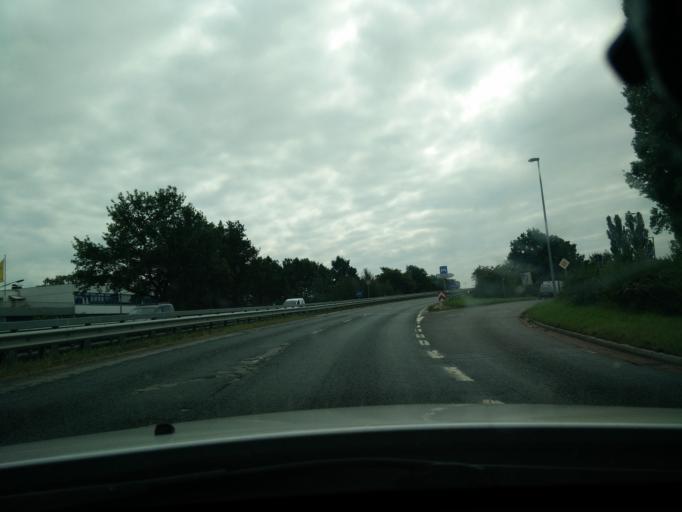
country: DE
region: Bremen
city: Bremen
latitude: 53.0602
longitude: 8.8801
